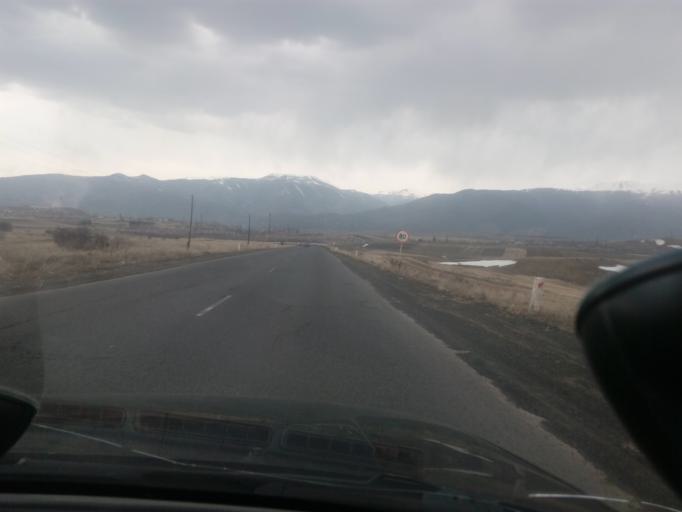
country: AM
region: Kotayk'i Marz
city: Fantan
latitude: 40.4039
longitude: 44.6763
